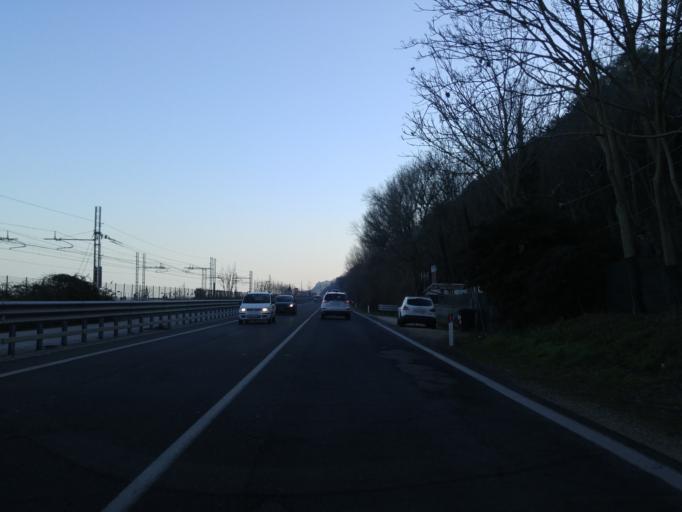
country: IT
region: The Marches
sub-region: Provincia di Pesaro e Urbino
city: Pesaro
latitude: 43.8927
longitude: 12.9465
